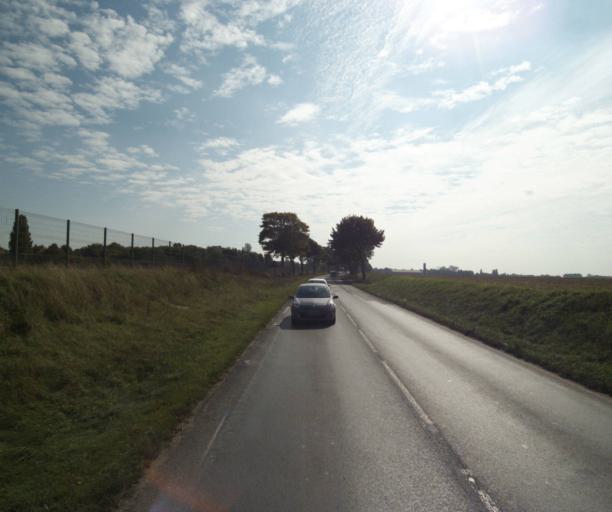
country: FR
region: Nord-Pas-de-Calais
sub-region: Departement du Nord
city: Seclin
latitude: 50.5671
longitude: 3.0240
